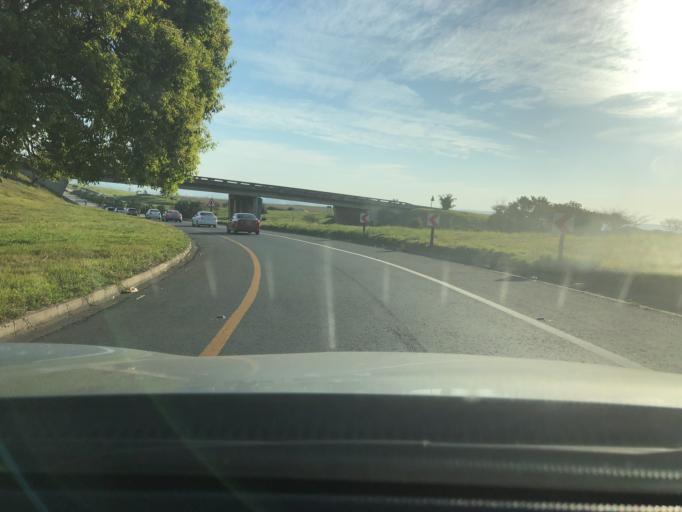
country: ZA
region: KwaZulu-Natal
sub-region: iLembe District Municipality
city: Stanger
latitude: -29.3459
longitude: 31.3247
